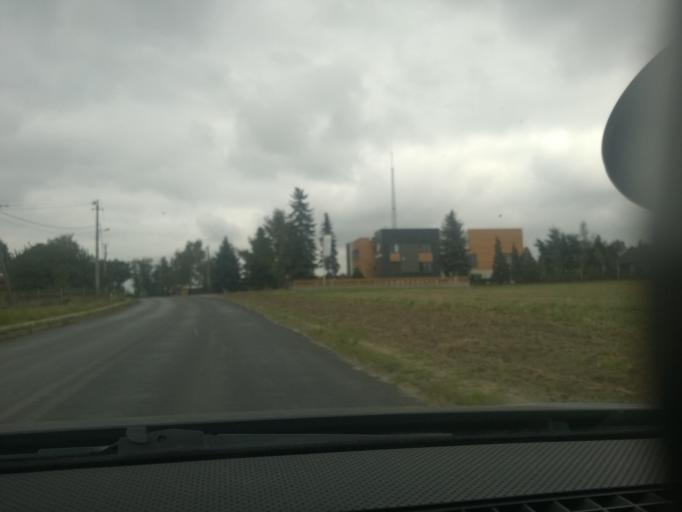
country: PL
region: Greater Poland Voivodeship
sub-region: Kalisz
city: Kalisz
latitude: 51.7262
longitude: 18.1305
